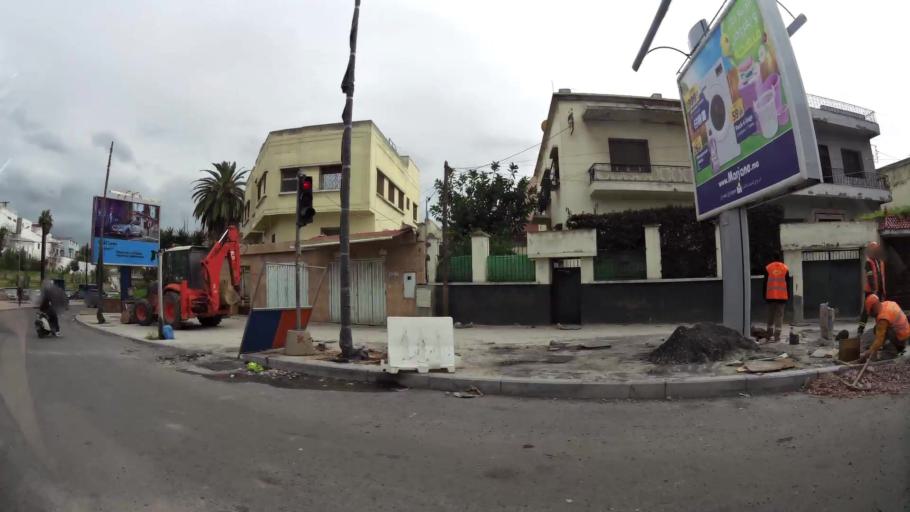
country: MA
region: Grand Casablanca
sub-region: Casablanca
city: Casablanca
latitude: 33.5690
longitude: -7.6118
